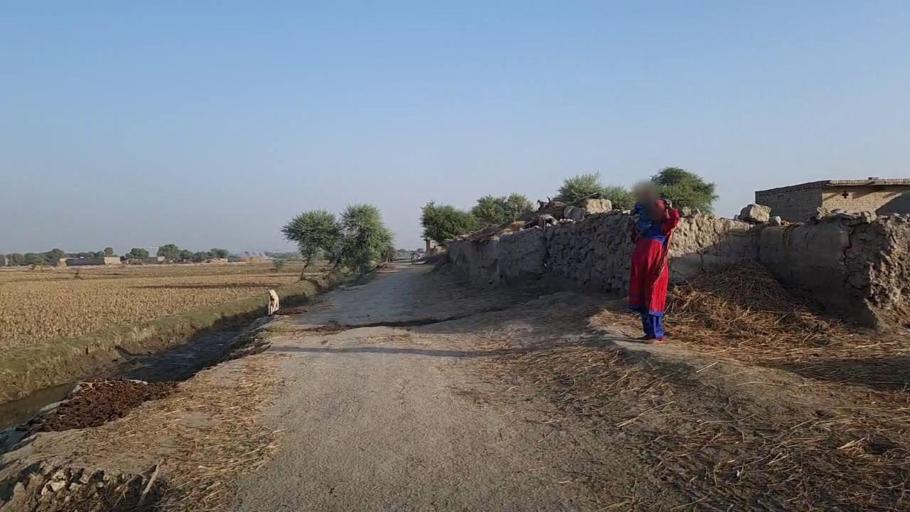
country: PK
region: Sindh
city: Kashmor
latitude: 28.4286
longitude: 69.4447
